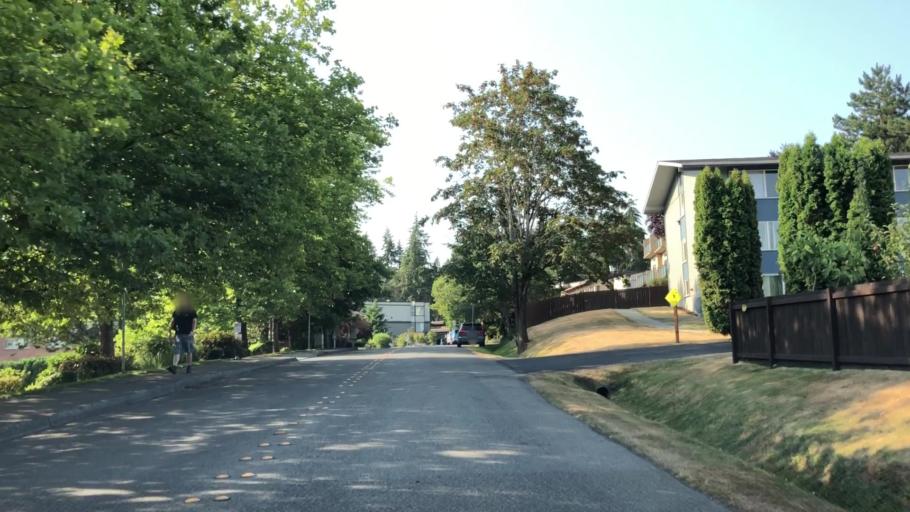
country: US
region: Washington
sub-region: King County
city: Sammamish
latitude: 47.6457
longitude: -122.1066
